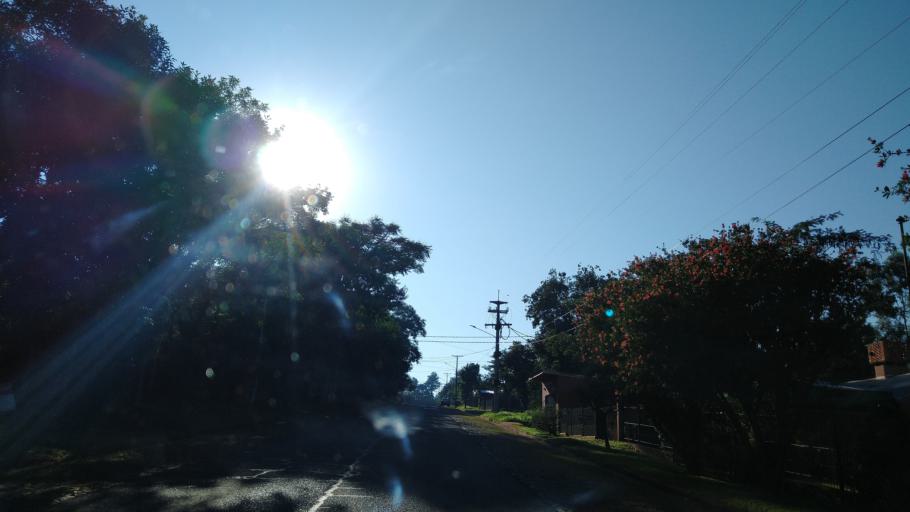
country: AR
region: Misiones
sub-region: Departamento de Montecarlo
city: Montecarlo
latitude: -26.5718
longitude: -54.7547
